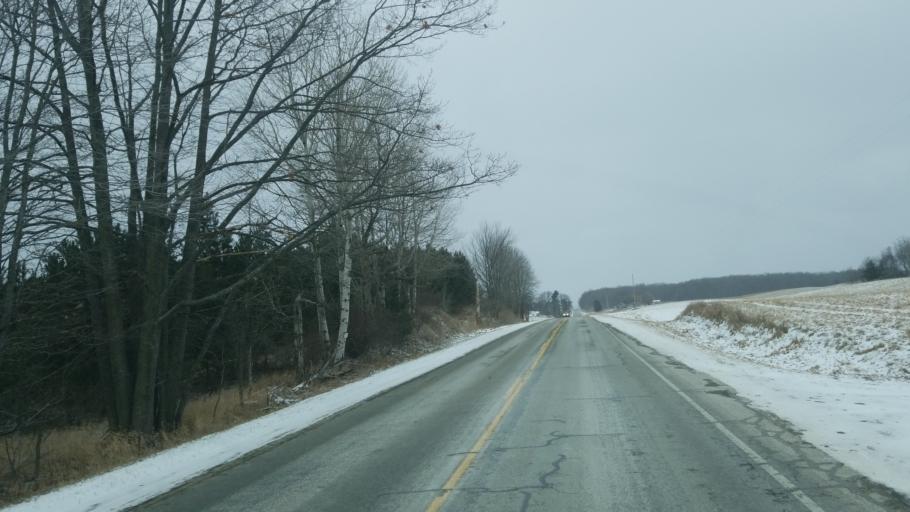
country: US
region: Michigan
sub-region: Osceola County
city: Evart
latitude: 43.9963
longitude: -85.2465
